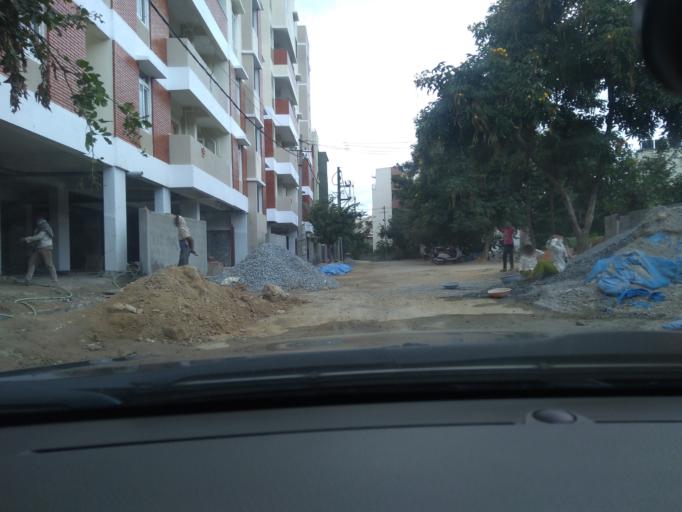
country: IN
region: Karnataka
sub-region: Bangalore Urban
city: Bangalore
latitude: 13.0074
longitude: 77.6616
